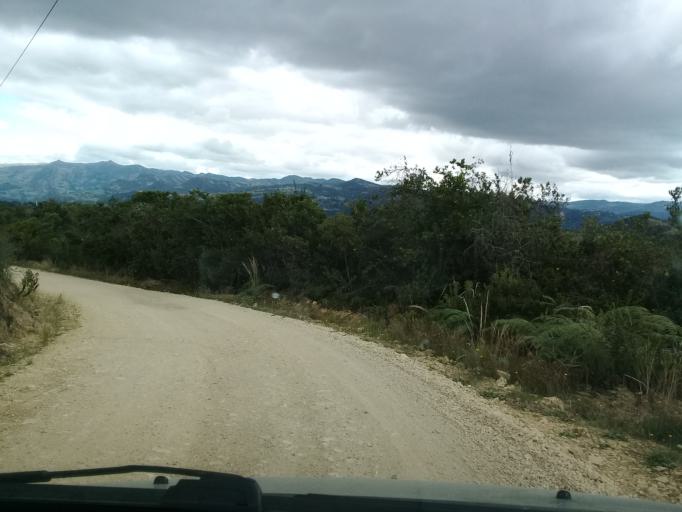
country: CO
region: Cundinamarca
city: Lenguazaque
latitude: 5.2835
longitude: -73.7417
